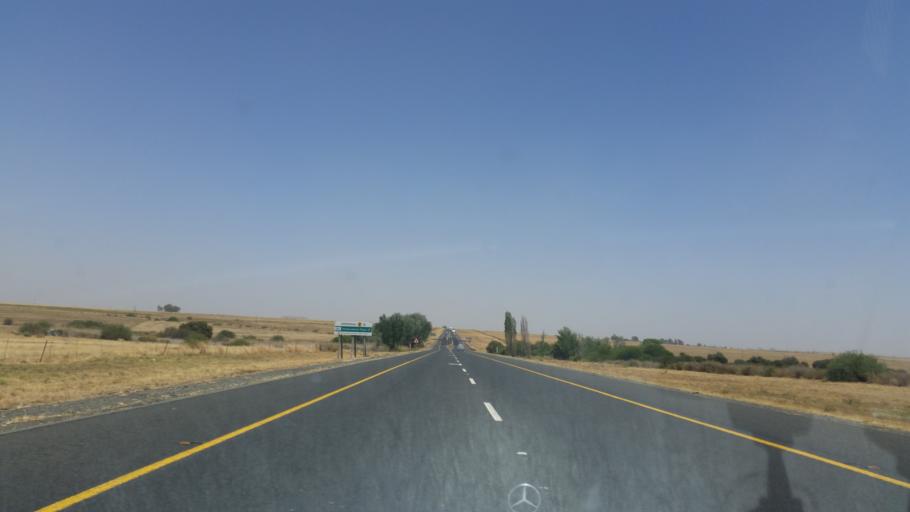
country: ZA
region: Orange Free State
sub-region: Lejweleputswa District Municipality
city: Brandfort
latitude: -28.7318
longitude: 26.7612
